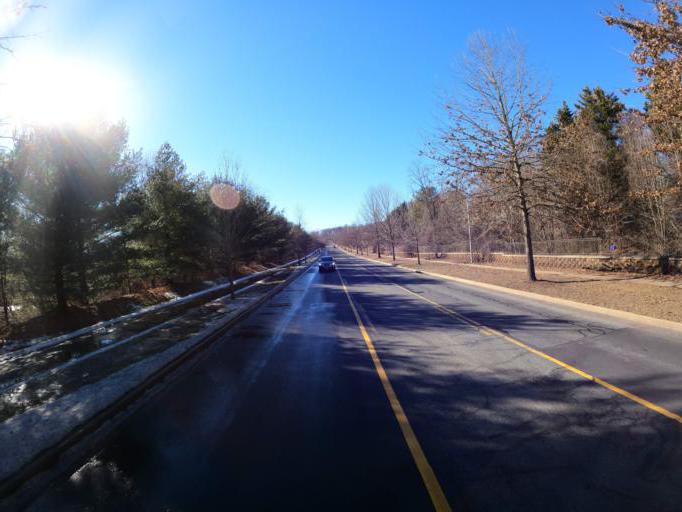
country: US
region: Maryland
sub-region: Montgomery County
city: Montgomery Village
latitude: 39.1914
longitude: -77.2294
